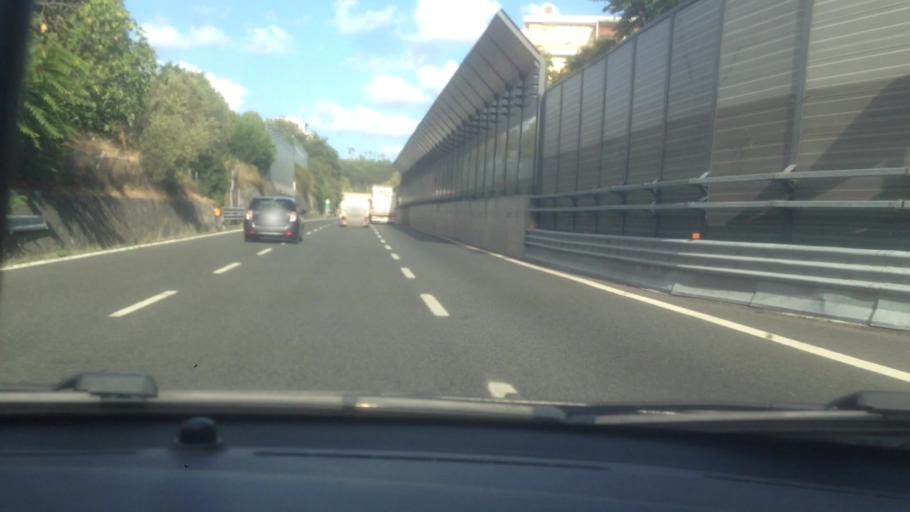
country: IT
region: Liguria
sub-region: Provincia di Genova
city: Cogoleto
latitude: 44.3916
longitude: 8.6479
